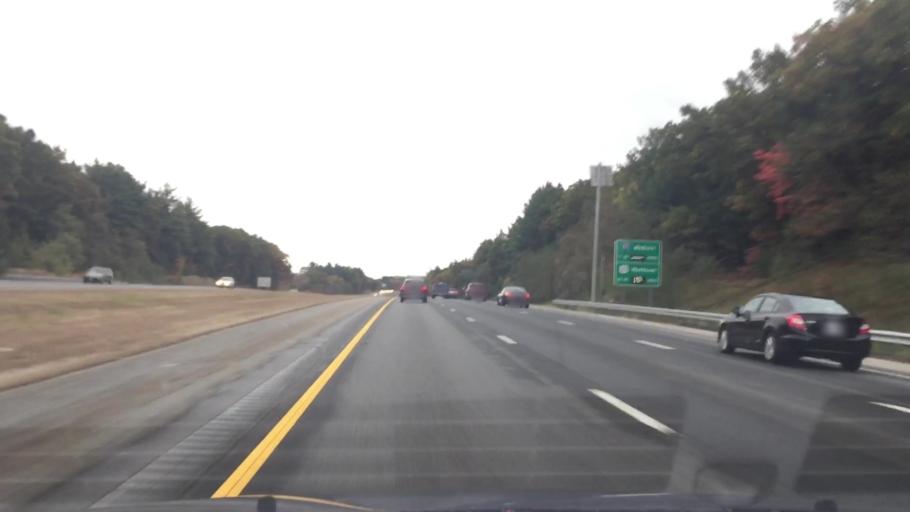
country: US
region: Massachusetts
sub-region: Middlesex County
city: Pinehurst
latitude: 42.4998
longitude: -71.2413
